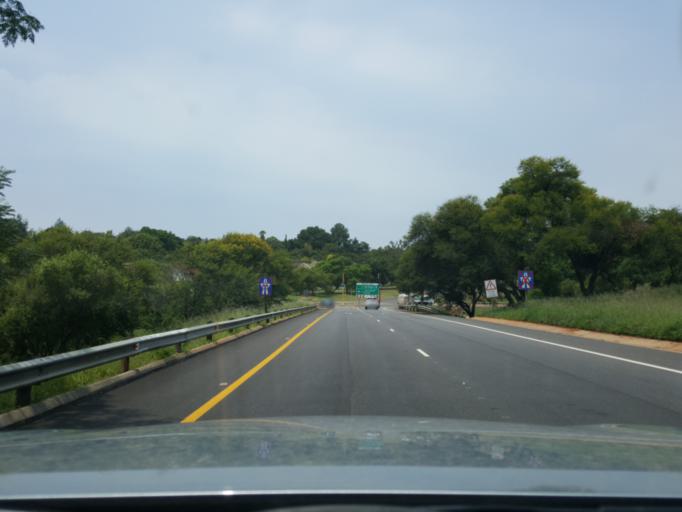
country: ZA
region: Gauteng
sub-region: City of Tshwane Metropolitan Municipality
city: Pretoria
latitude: -25.7524
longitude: 28.3029
